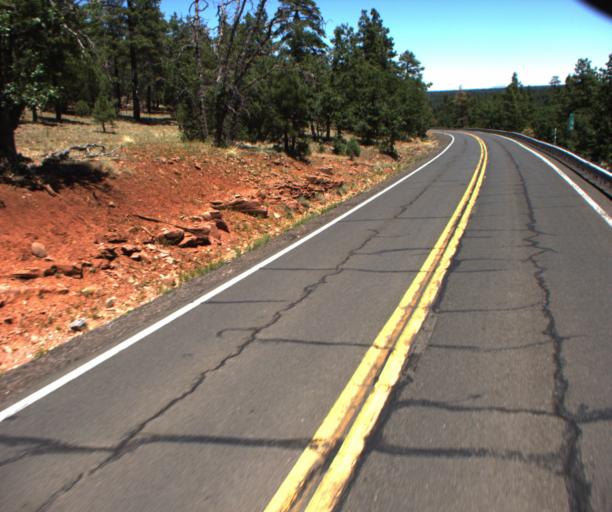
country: US
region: Arizona
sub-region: Gila County
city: Pine
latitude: 34.5959
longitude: -111.2440
